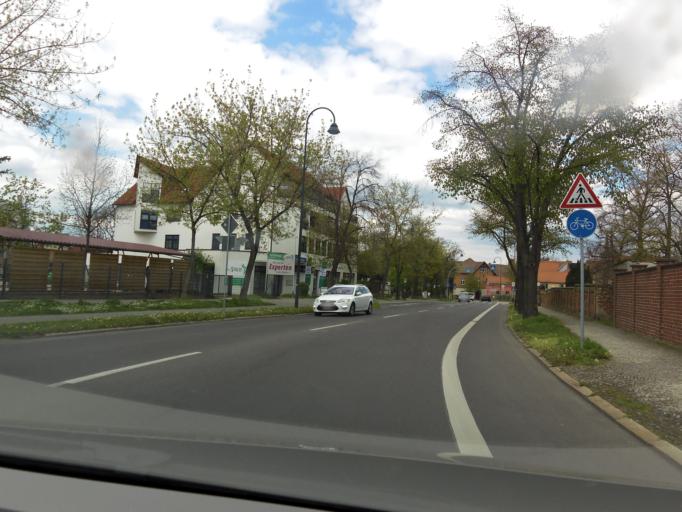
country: DE
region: Saxony-Anhalt
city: Naumburg
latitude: 51.1506
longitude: 11.7986
